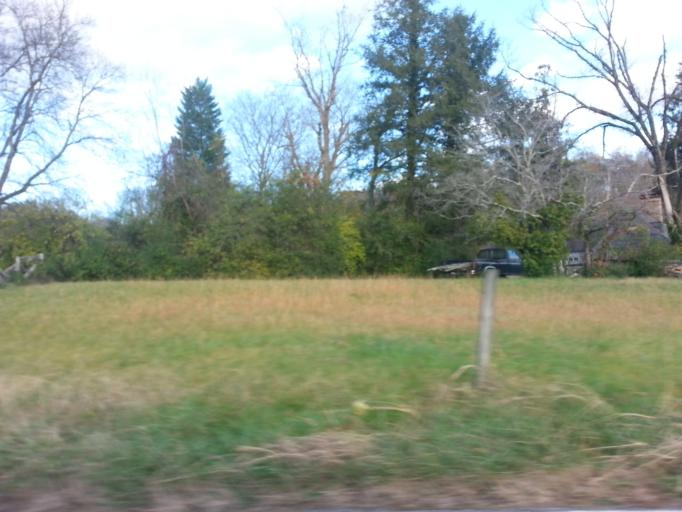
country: US
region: Tennessee
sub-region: Knox County
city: Knoxville
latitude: 35.9101
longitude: -83.9704
